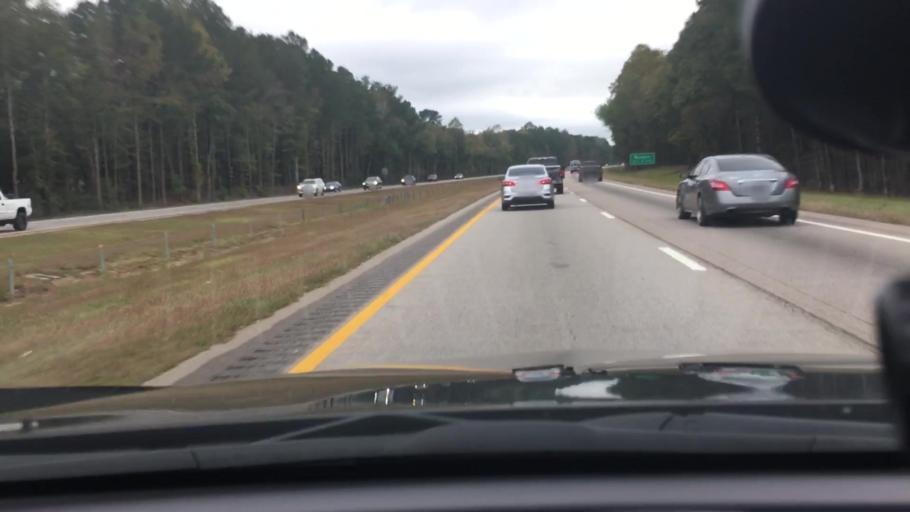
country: US
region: North Carolina
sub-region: Wake County
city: Zebulon
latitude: 35.8282
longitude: -78.3607
